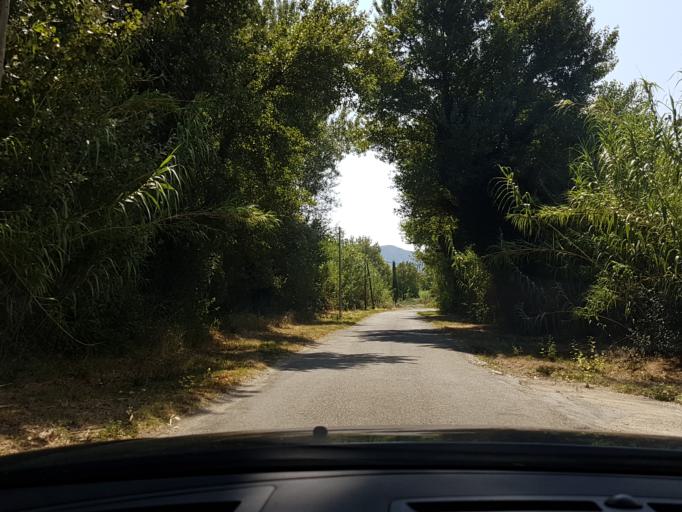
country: FR
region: Provence-Alpes-Cote d'Azur
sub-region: Departement des Bouches-du-Rhone
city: Saint-Remy-de-Provence
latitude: 43.7927
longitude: 4.8783
